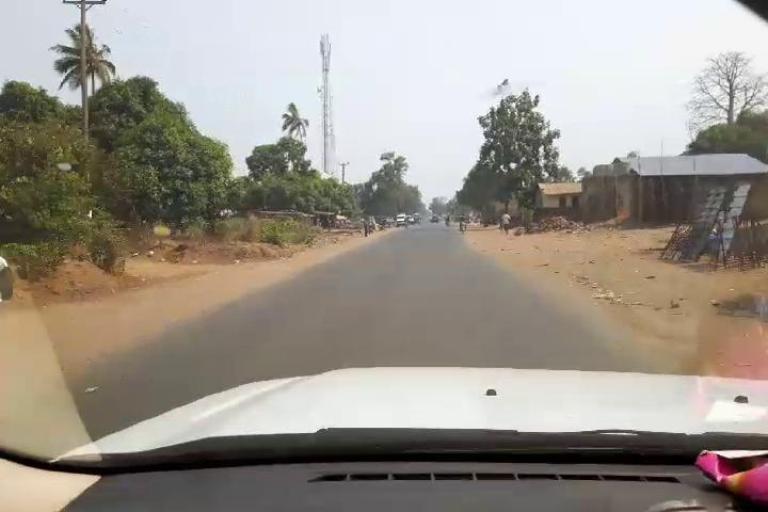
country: SL
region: Western Area
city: Waterloo
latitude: 8.3127
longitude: -13.0745
